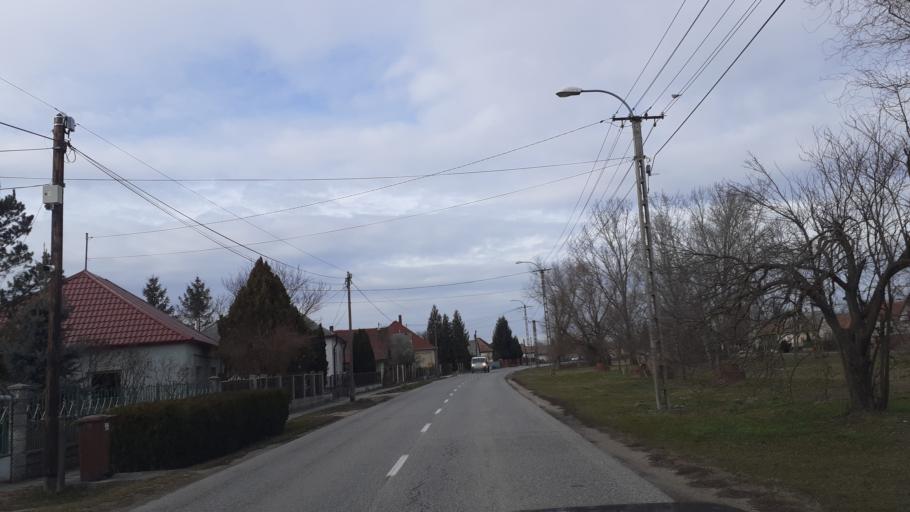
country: HU
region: Fejer
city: Szabadbattyan
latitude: 47.0766
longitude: 18.4137
